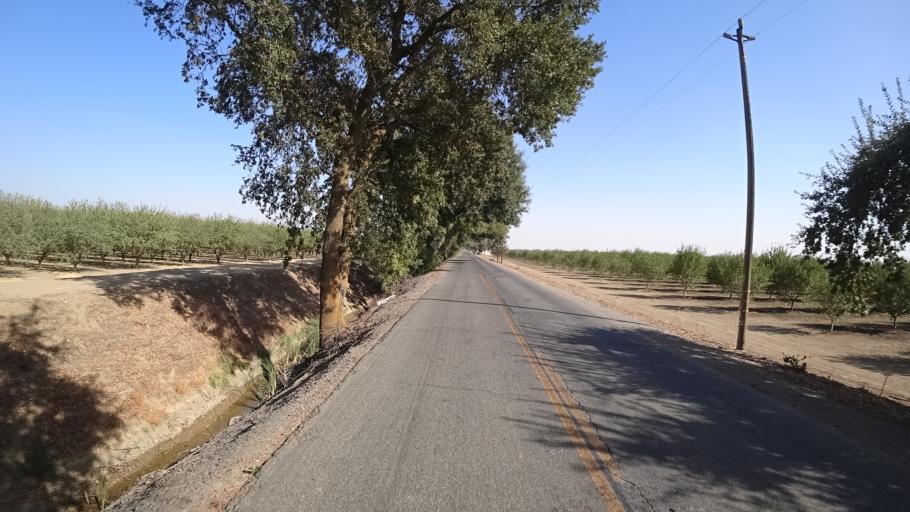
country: US
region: California
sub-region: Yolo County
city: Woodland
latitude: 38.7357
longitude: -121.8472
